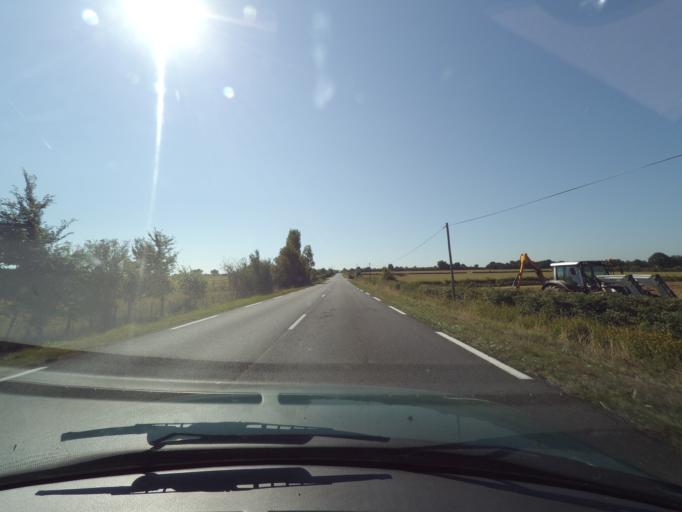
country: FR
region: Poitou-Charentes
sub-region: Departement de la Vienne
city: Lussac-les-Chateaux
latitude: 46.3729
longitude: 0.7607
